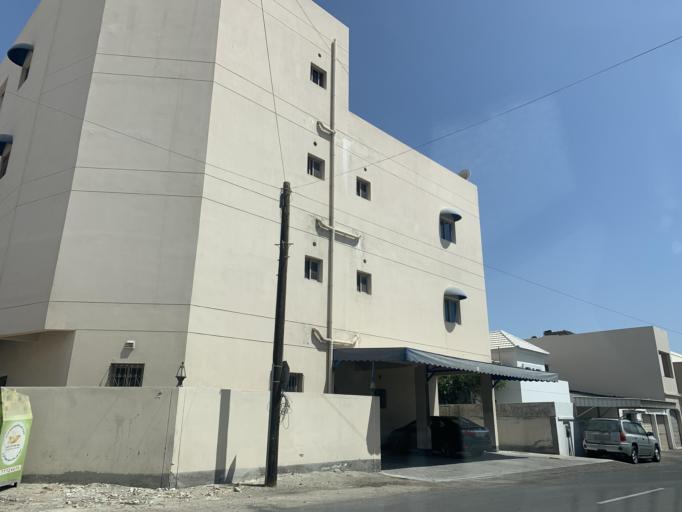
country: BH
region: Northern
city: Ar Rifa'
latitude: 26.1344
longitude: 50.5789
